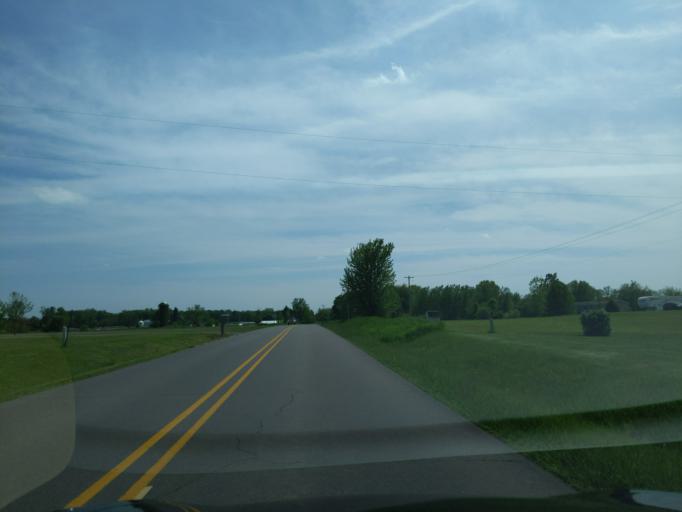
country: US
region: Michigan
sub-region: Ingham County
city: Leslie
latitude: 42.4162
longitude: -84.3127
